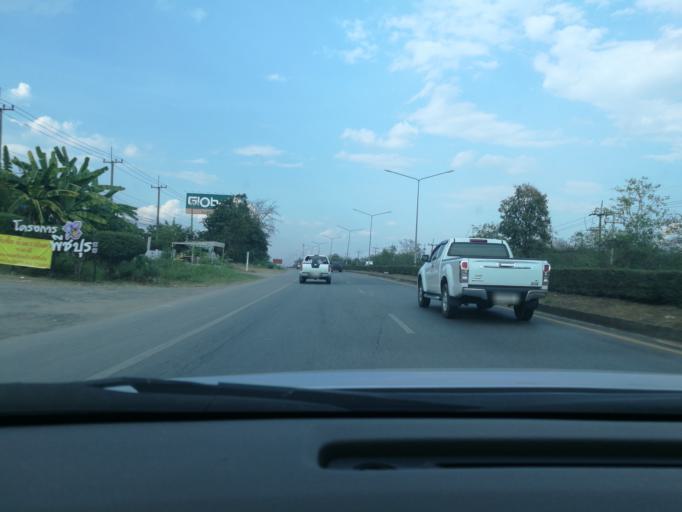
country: TH
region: Phetchabun
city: Phetchabun
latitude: 16.4715
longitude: 101.1587
